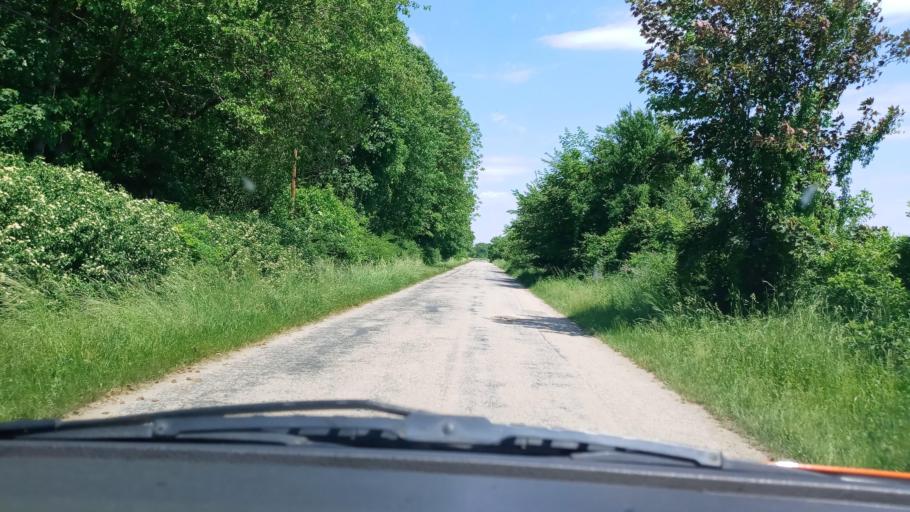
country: HR
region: Osjecko-Baranjska
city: Viljevo
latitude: 45.8225
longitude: 18.0880
